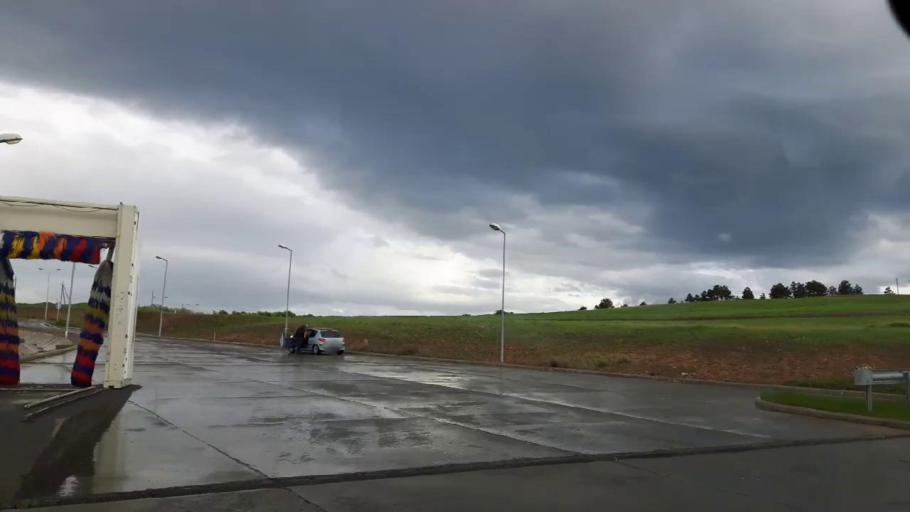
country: GE
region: Shida Kartli
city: Gori
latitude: 42.0147
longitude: 44.0318
